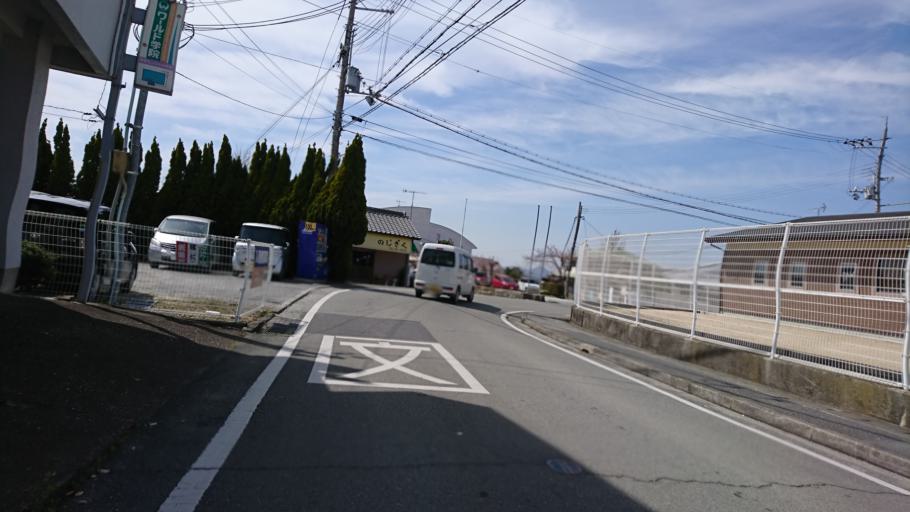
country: JP
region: Hyogo
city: Kakogawacho-honmachi
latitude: 34.7489
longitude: 134.9024
